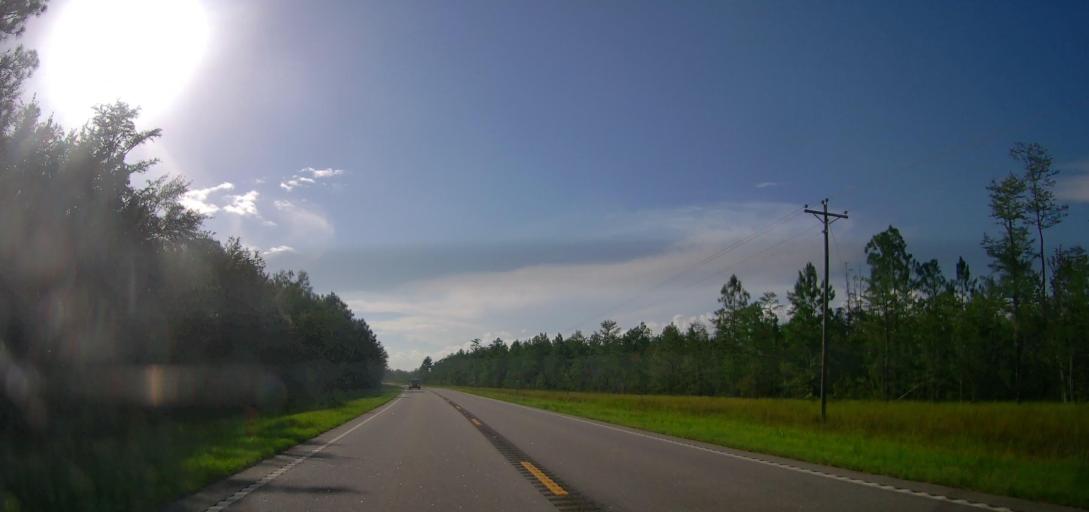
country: US
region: Georgia
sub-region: Coffee County
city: Nicholls
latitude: 31.4541
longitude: -82.7330
